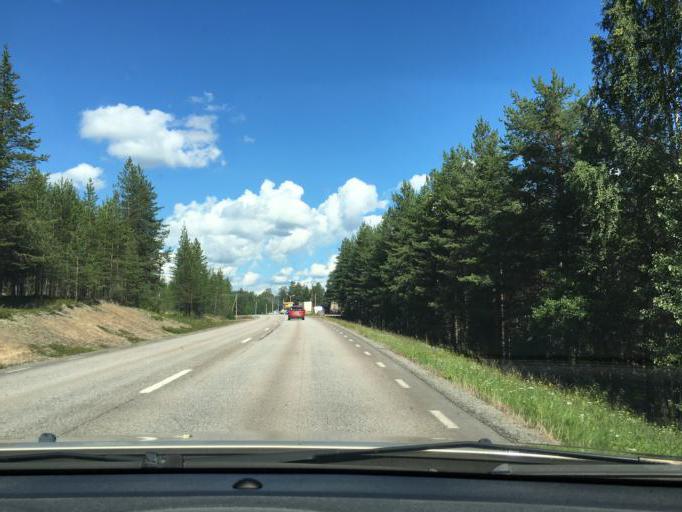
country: SE
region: Norrbotten
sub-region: Overkalix Kommun
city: OEverkalix
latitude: 66.2924
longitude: 22.8172
